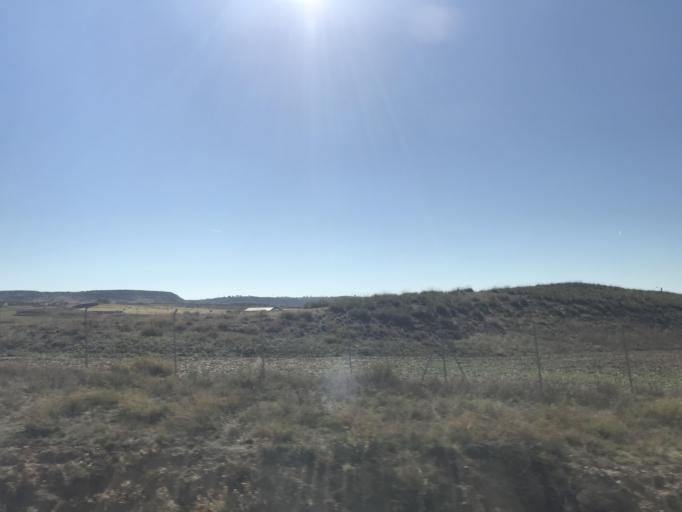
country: ES
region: Madrid
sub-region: Provincia de Madrid
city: Torres de la Alameda
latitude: 40.4294
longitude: -3.3694
